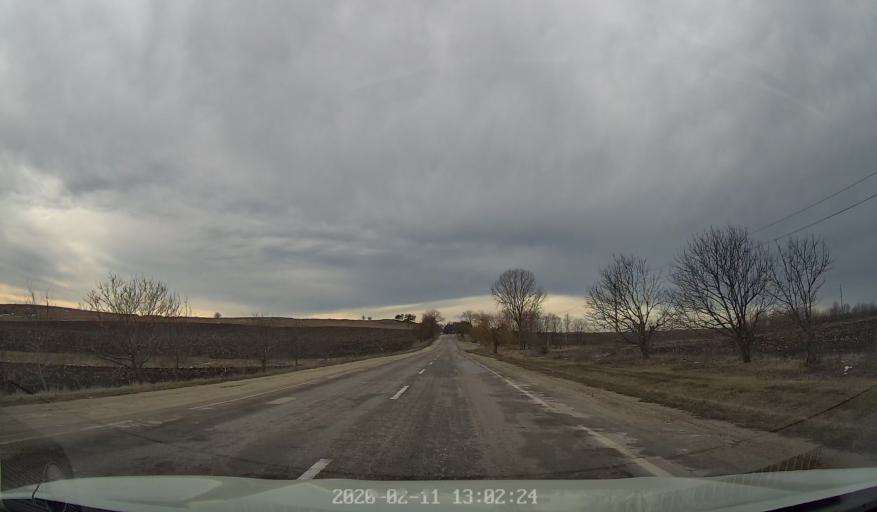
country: MD
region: Briceni
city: Briceni
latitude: 48.3165
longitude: 26.9816
